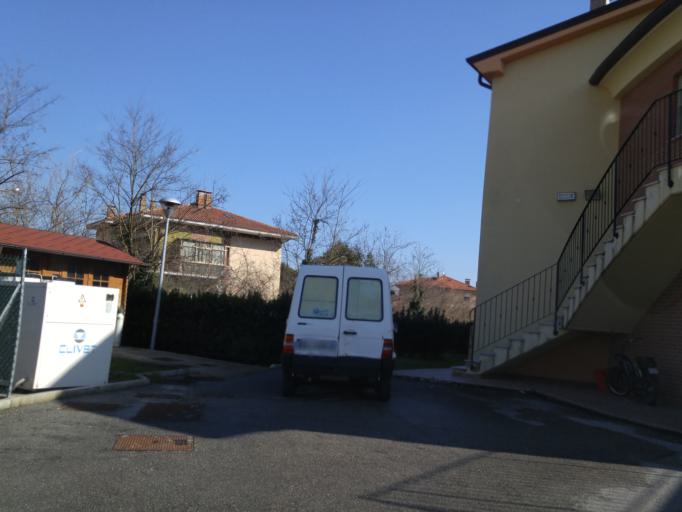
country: IT
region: The Marches
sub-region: Provincia di Pesaro e Urbino
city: Fossombrone
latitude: 43.6841
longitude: 12.8011
